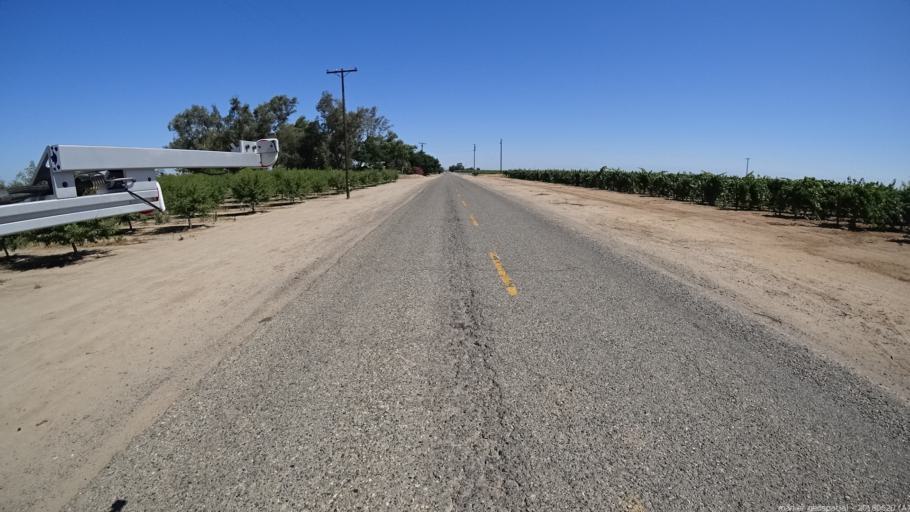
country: US
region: California
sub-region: Madera County
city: Parkwood
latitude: 36.8866
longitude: -120.0195
